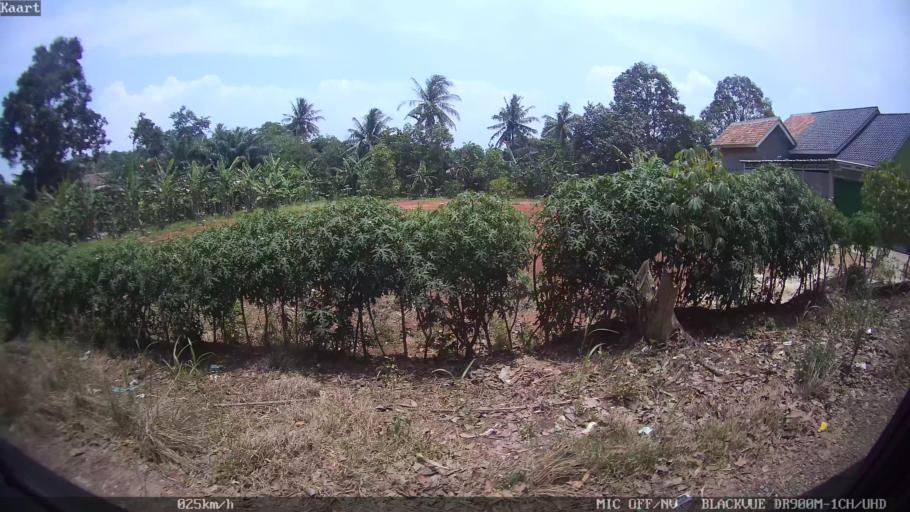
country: ID
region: Lampung
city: Natar
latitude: -5.3175
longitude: 105.2484
